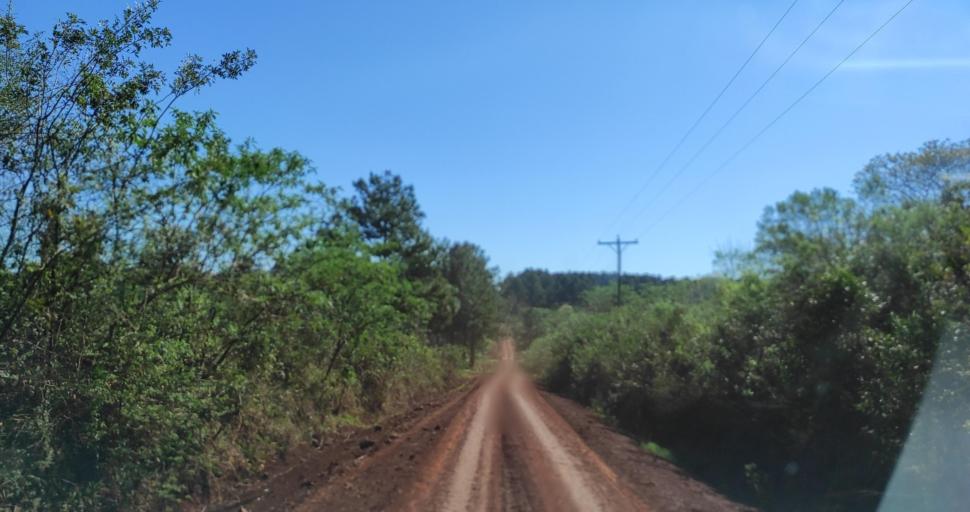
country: AR
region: Misiones
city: Capiovi
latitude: -26.9167
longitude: -55.0269
